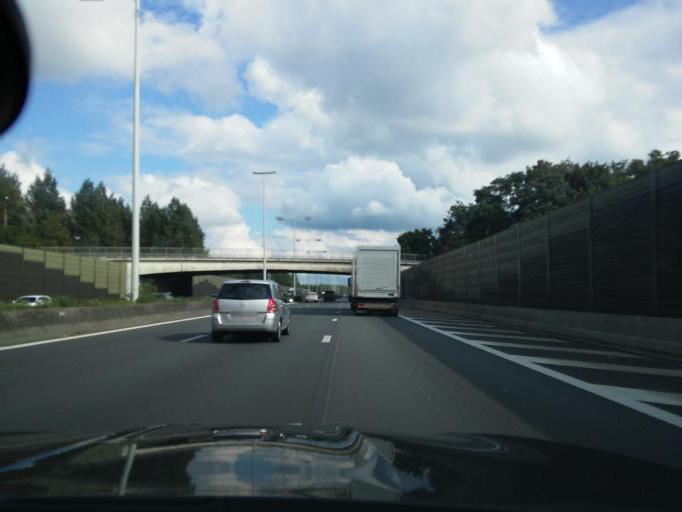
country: BE
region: Flanders
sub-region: Provincie Oost-Vlaanderen
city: Aalst
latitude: 50.9138
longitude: 4.0478
